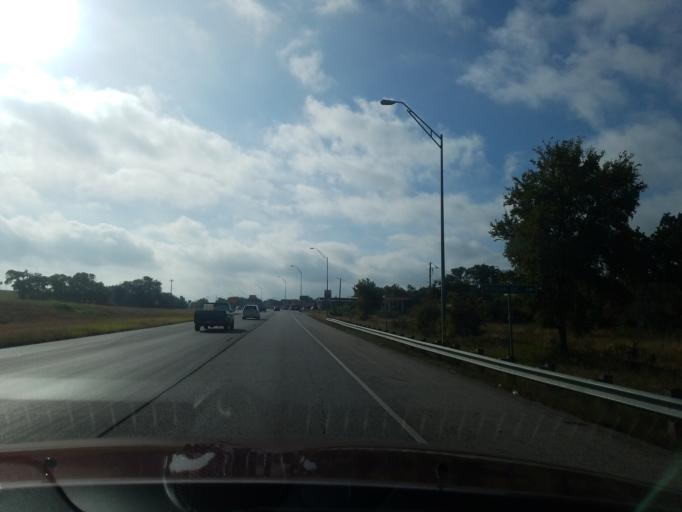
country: US
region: Texas
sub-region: Williamson County
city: Cedar Park
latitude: 30.4839
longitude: -97.8063
